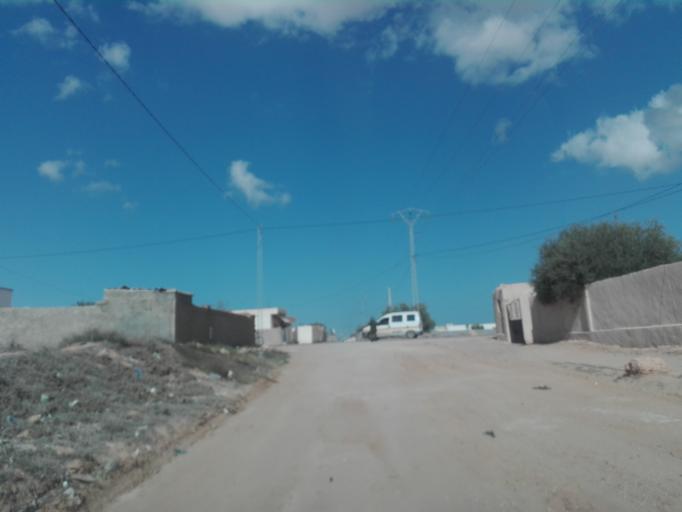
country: TN
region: Madanin
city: Bin Qirdan
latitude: 33.1526
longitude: 11.1930
